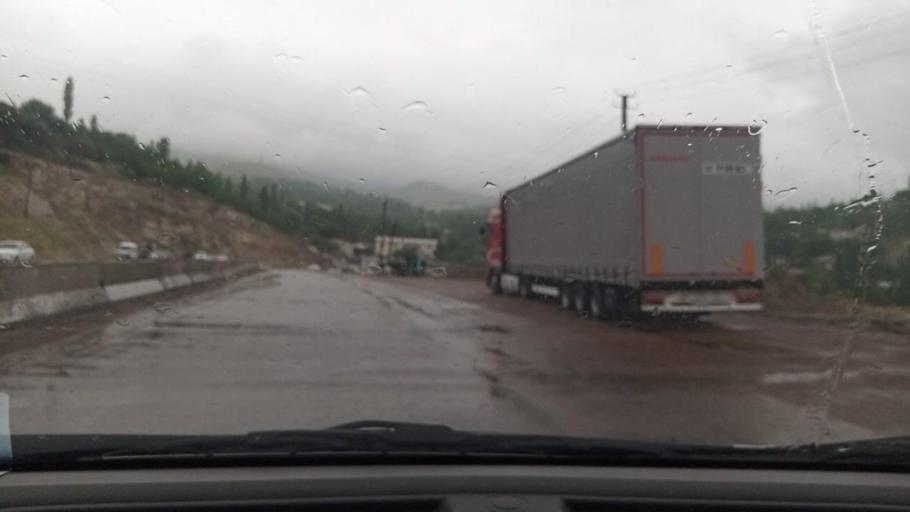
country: UZ
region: Toshkent
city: Angren
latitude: 41.0724
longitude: 70.2520
